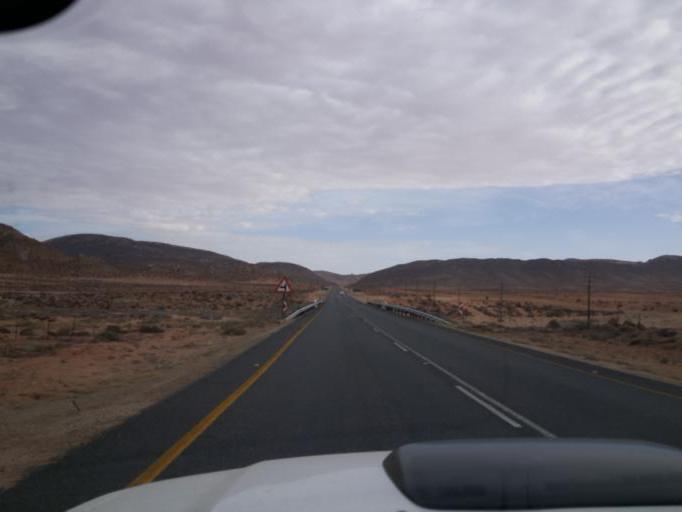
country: ZA
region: Northern Cape
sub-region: Namakwa District Municipality
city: Springbok
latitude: -29.4732
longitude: 17.8373
